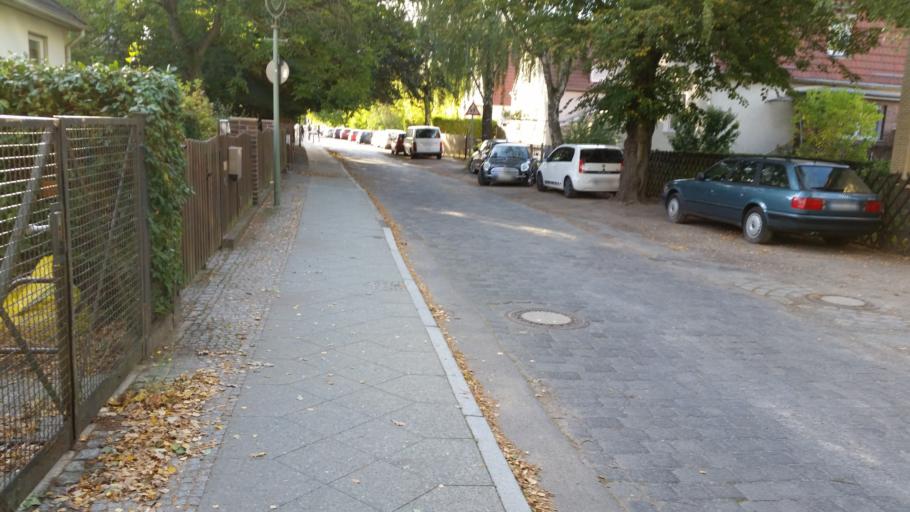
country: DE
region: Berlin
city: Lichtenrade
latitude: 52.4115
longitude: 13.4099
